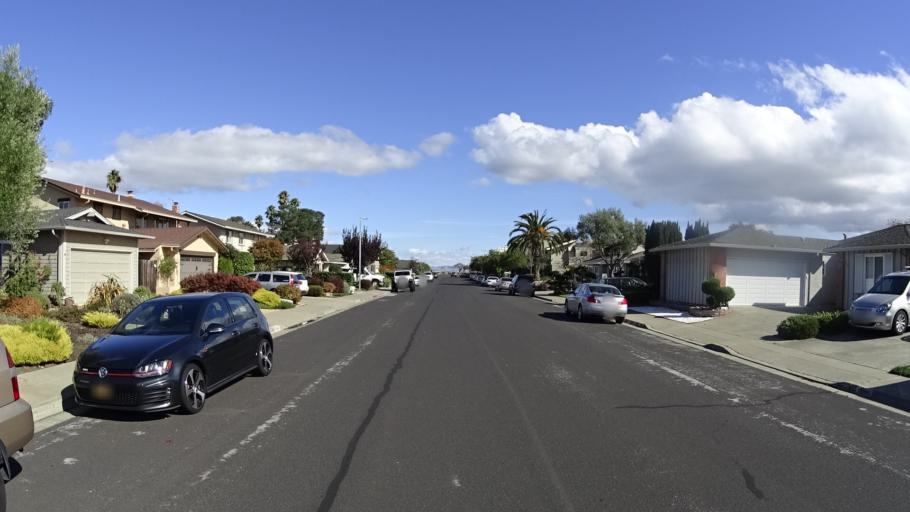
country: US
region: California
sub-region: San Mateo County
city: Foster City
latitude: 37.5603
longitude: -122.2520
